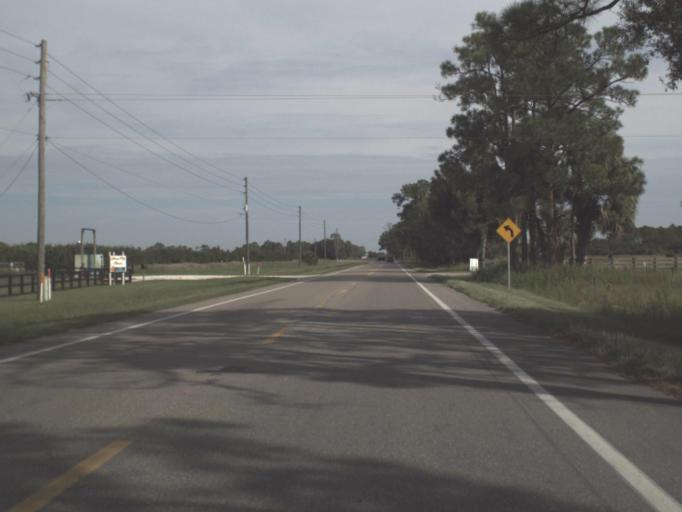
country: US
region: Florida
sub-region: DeSoto County
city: Nocatee
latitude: 27.0136
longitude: -81.7604
